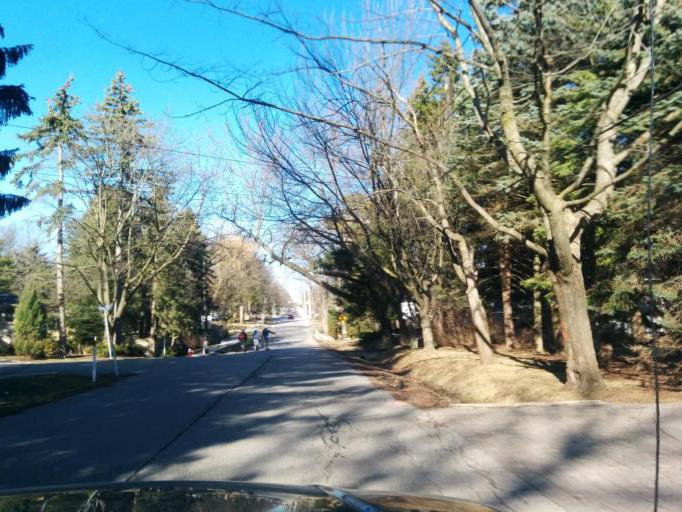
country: CA
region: Ontario
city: Mississauga
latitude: 43.5600
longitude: -79.5925
